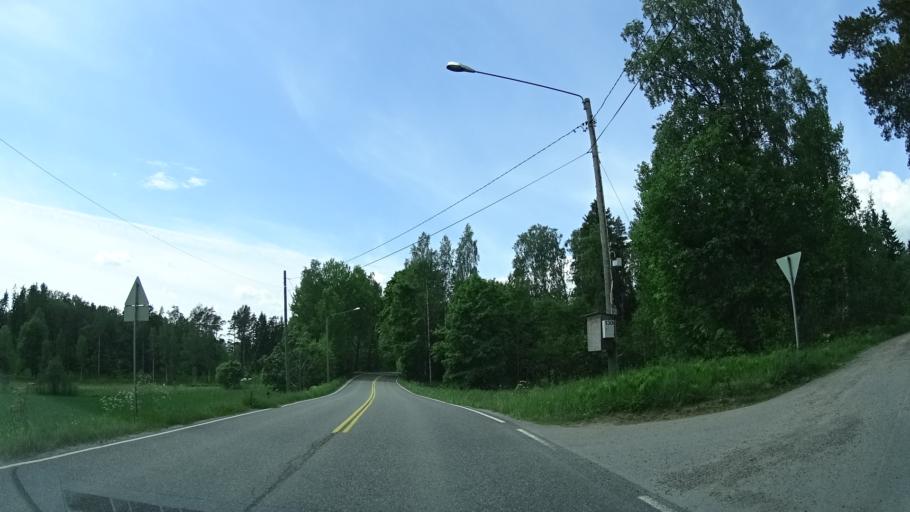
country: FI
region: Uusimaa
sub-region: Helsinki
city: Kirkkonummi
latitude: 60.2163
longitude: 24.4811
